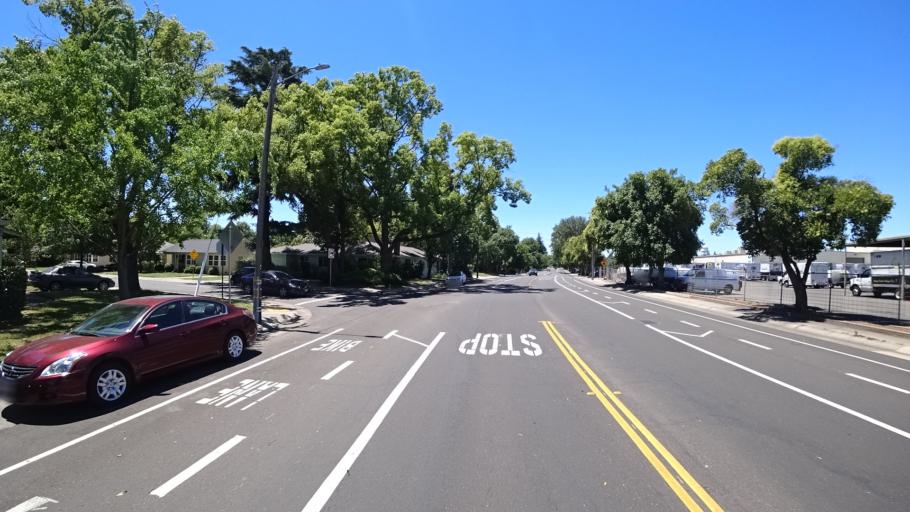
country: US
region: California
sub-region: Sacramento County
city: Sacramento
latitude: 38.5818
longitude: -121.4502
